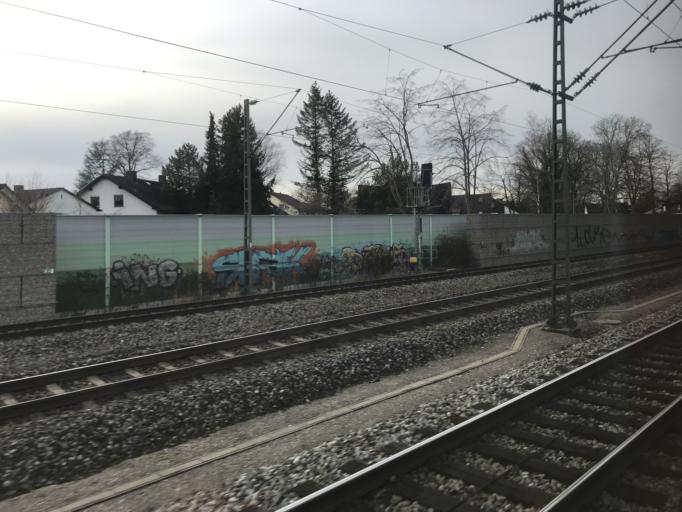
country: DE
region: Bavaria
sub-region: Upper Bavaria
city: Grobenzell
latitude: 48.1967
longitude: 11.3710
